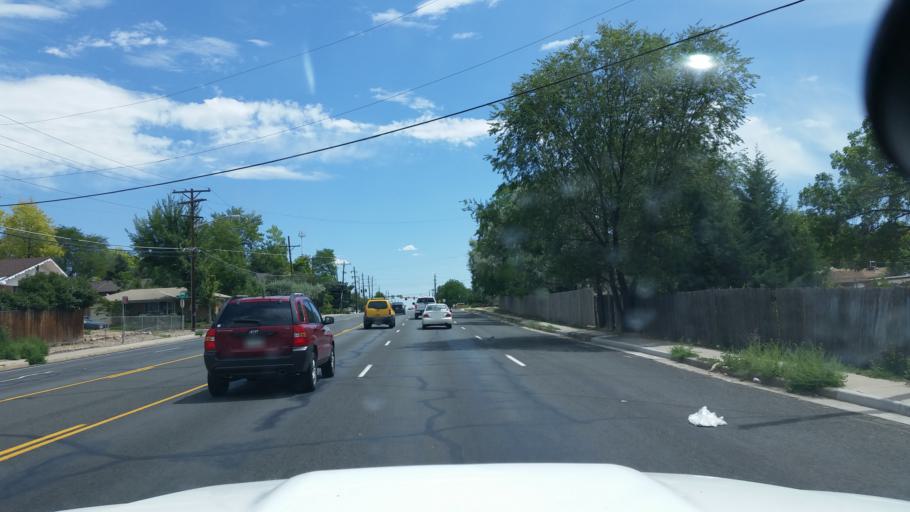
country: US
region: Colorado
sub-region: Adams County
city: Westminster
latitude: 39.8635
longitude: -105.0286
